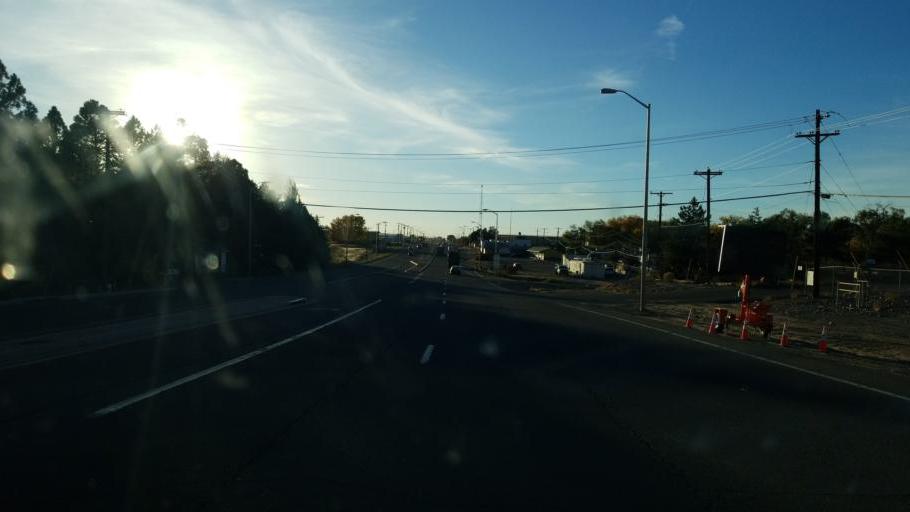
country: US
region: New Mexico
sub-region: San Juan County
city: Farmington
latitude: 36.7191
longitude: -108.1597
